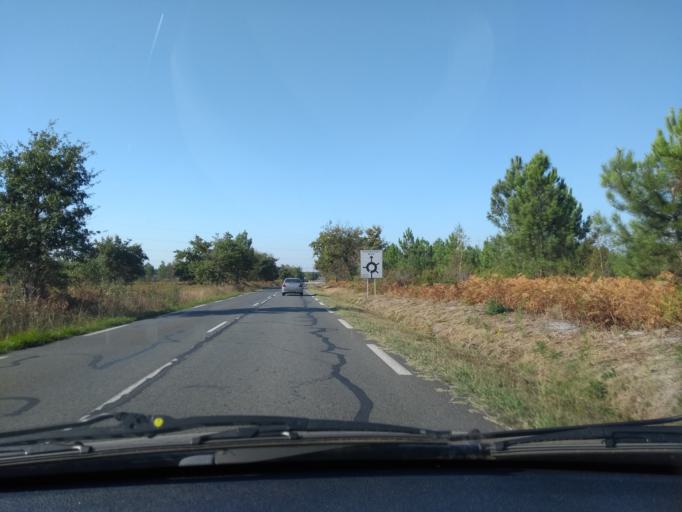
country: FR
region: Aquitaine
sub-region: Departement de la Gironde
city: Mios
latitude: 44.6193
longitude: -0.9143
